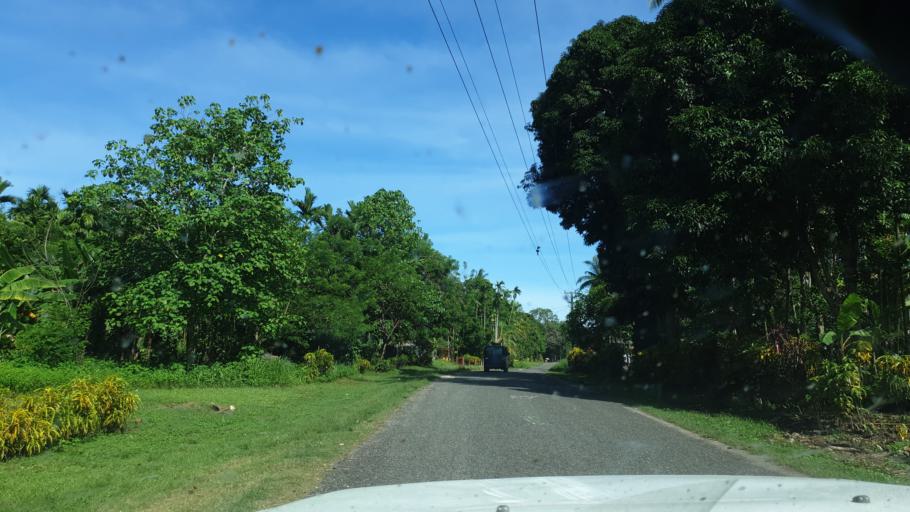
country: PG
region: Madang
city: Madang
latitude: -4.8096
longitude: 145.7531
